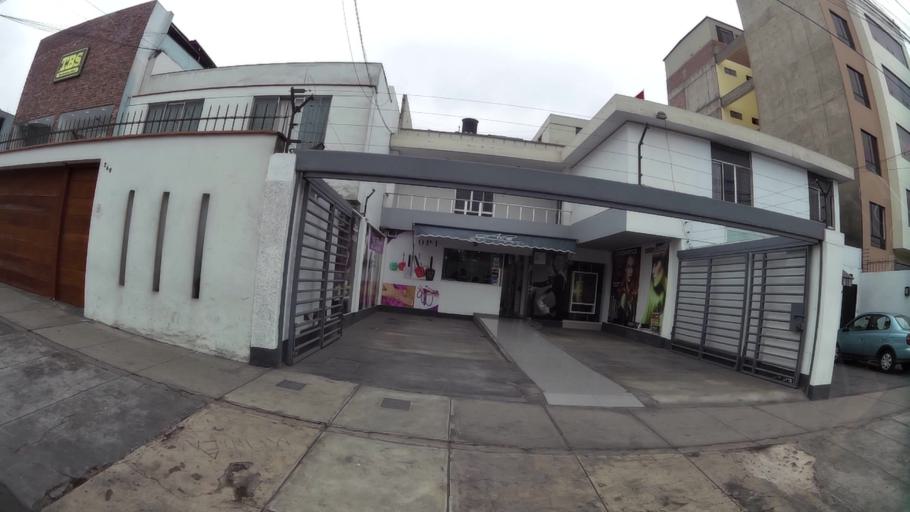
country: PE
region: Lima
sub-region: Lima
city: La Molina
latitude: -12.1076
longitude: -76.9742
